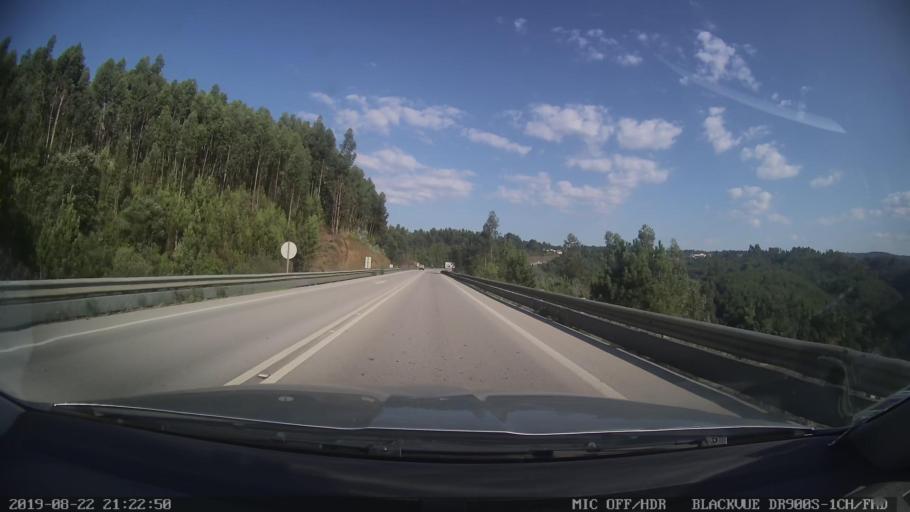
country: PT
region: Castelo Branco
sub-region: Serta
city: Serta
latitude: 39.8231
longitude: -8.1039
